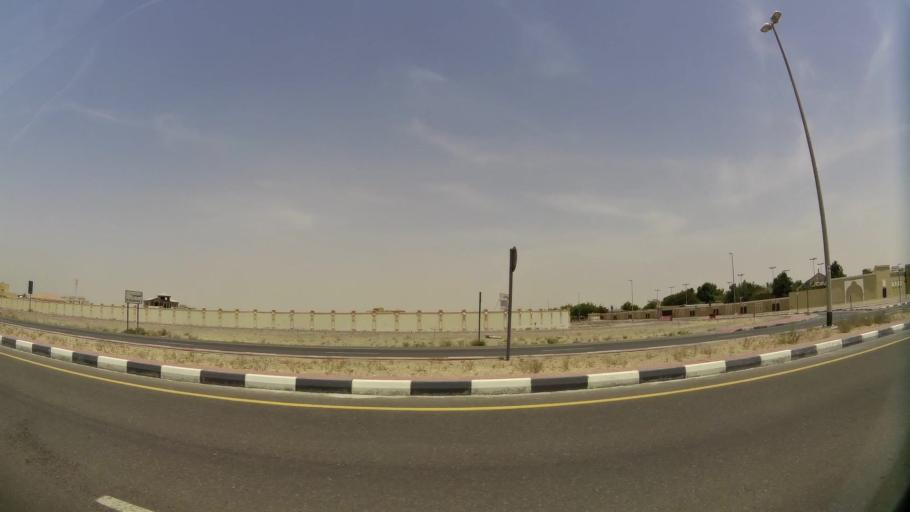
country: AE
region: Ash Shariqah
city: Sharjah
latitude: 25.2440
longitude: 55.4680
